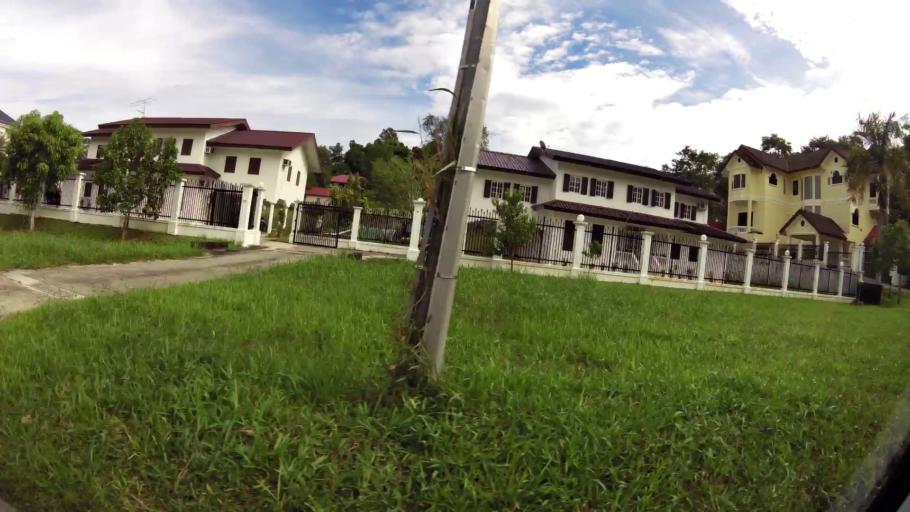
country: BN
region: Brunei and Muara
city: Bandar Seri Begawan
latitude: 4.8915
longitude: 114.8954
